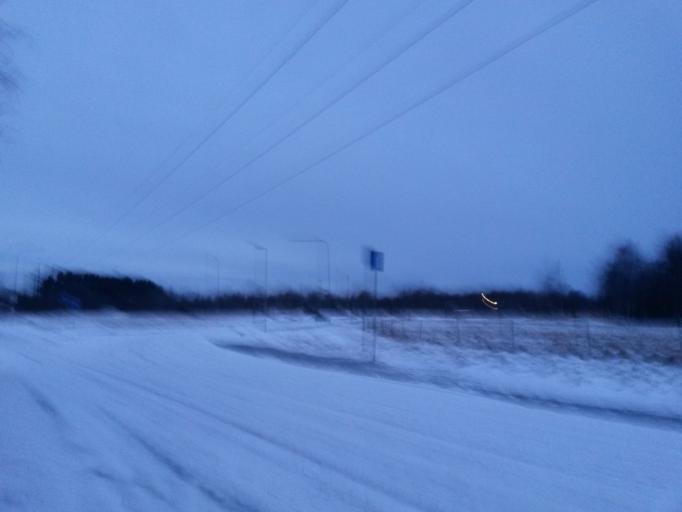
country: SE
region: Vaesterbotten
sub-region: Umea Kommun
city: Roback
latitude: 63.8415
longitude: 20.2164
